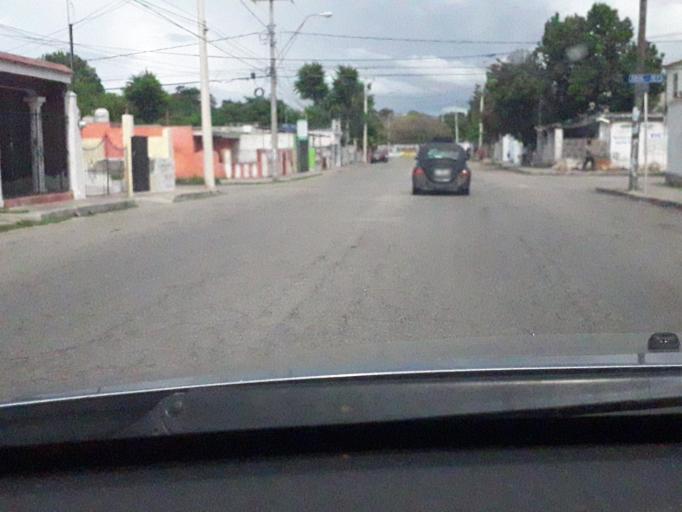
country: MX
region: Yucatan
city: Merida
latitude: 20.9708
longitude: -89.6575
